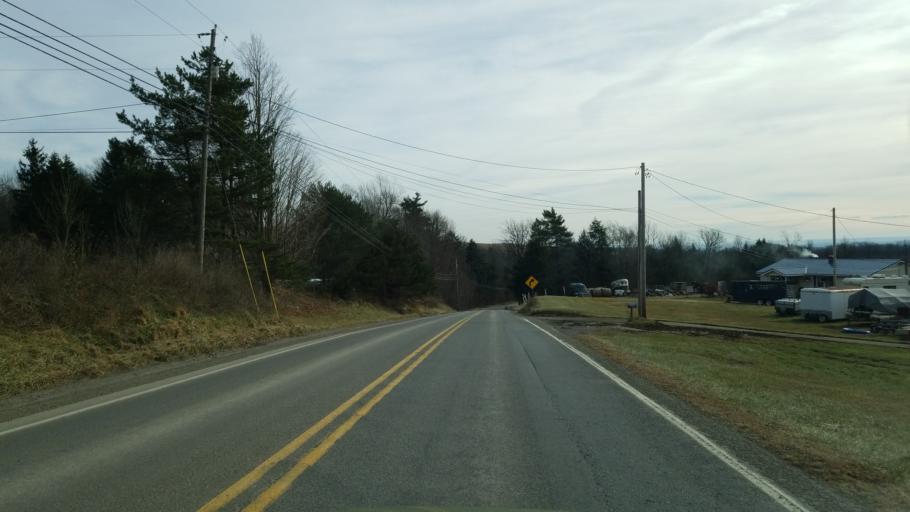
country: US
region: Pennsylvania
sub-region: Indiana County
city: Johnsonburg
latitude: 40.9126
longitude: -78.8171
